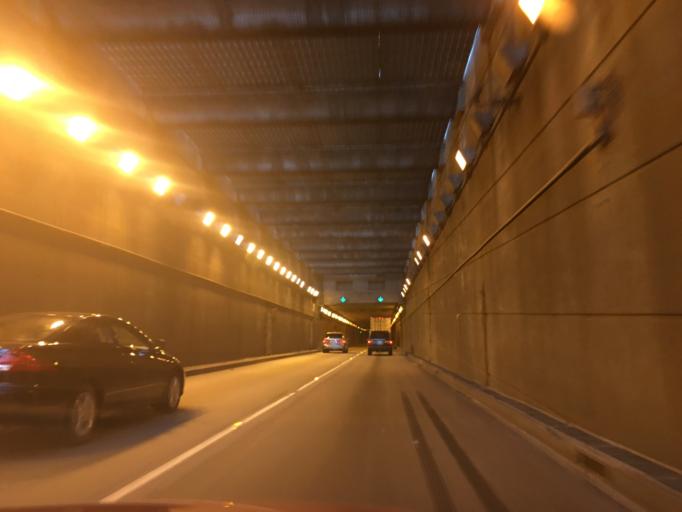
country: CA
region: British Columbia
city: Ladner
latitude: 49.1244
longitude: -123.0790
